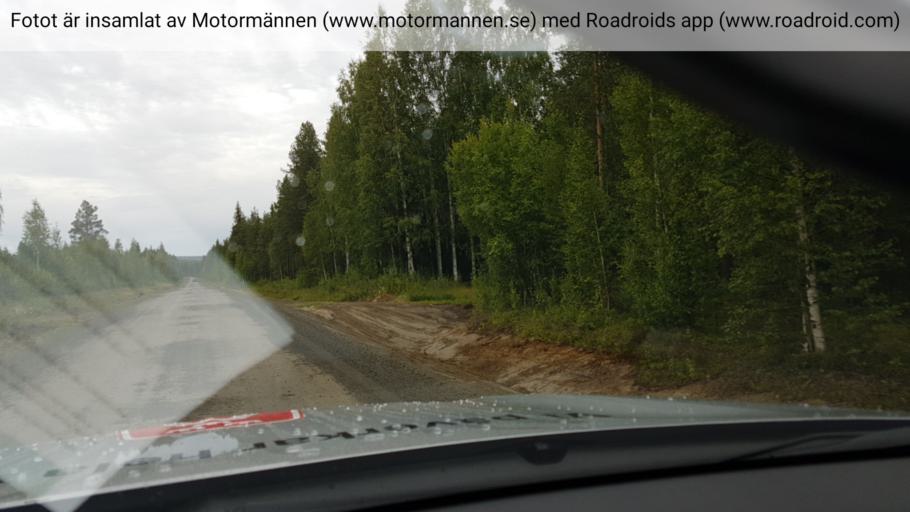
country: SE
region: Norrbotten
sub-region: Alvsbyns Kommun
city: AElvsbyn
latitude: 65.9269
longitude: 21.2564
